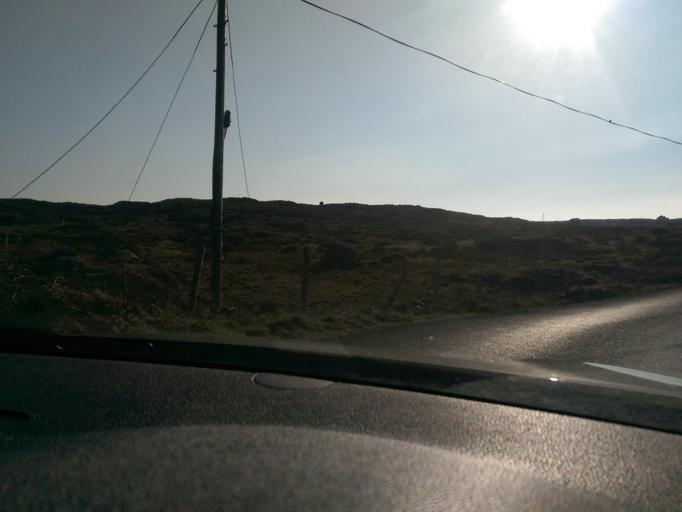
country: IE
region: Connaught
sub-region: County Galway
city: Clifden
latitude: 53.3673
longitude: -9.8608
